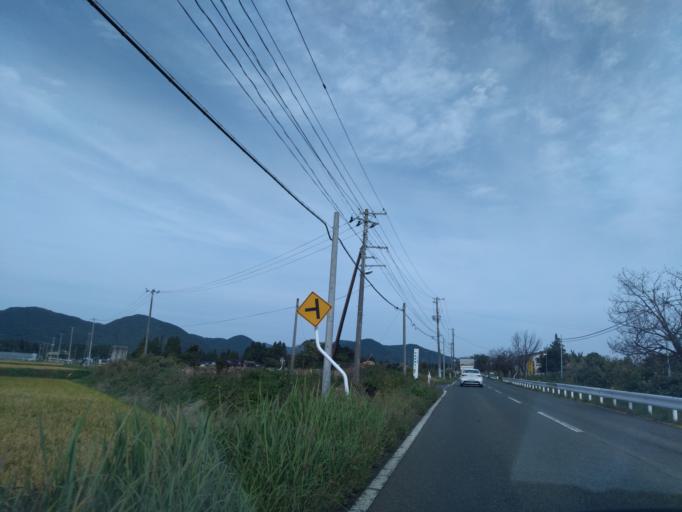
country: JP
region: Iwate
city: Hanamaki
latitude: 39.4283
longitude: 141.0842
